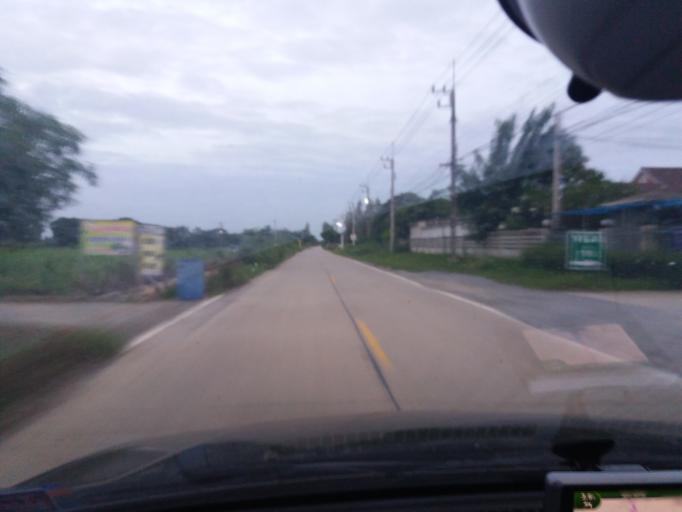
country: TH
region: Suphan Buri
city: Ban Sam Chuk
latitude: 14.7344
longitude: 100.0893
